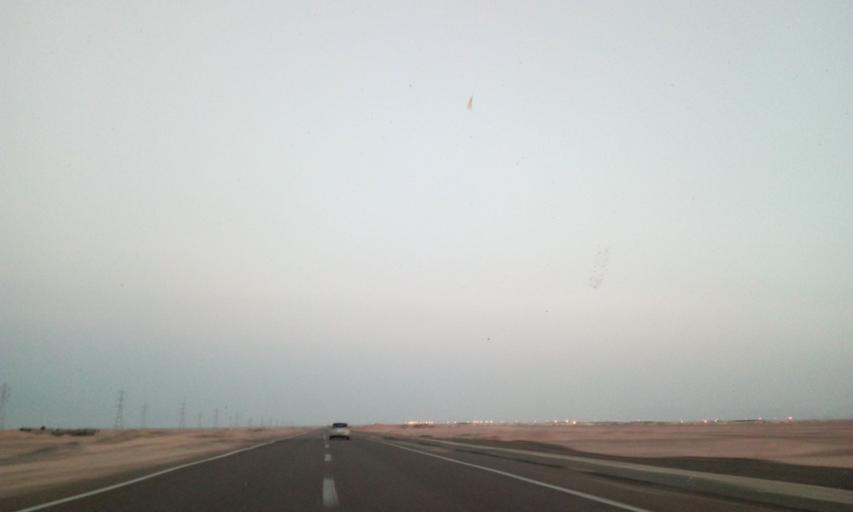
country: EG
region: Red Sea
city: Hurghada
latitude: 27.2224
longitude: 33.7074
